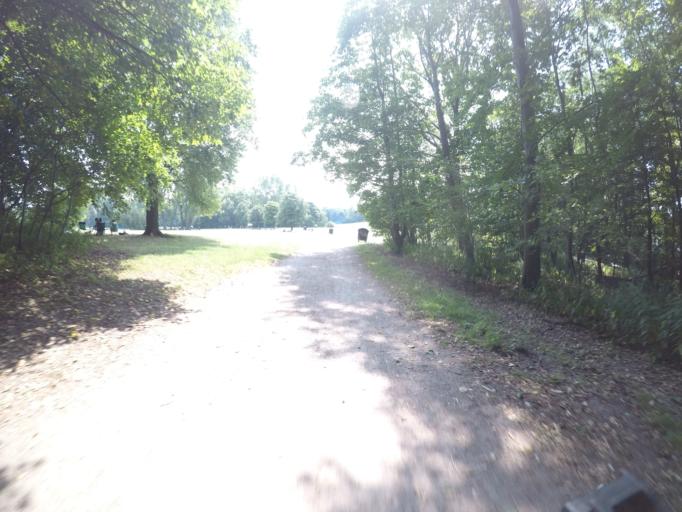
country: DE
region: Schleswig-Holstein
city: Barsbuettel
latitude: 53.5599
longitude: 10.1451
